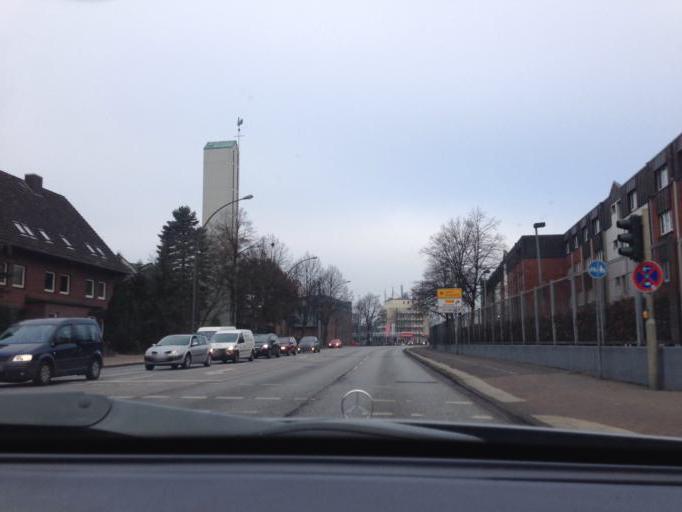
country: DE
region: Hamburg
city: Farmsen-Berne
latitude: 53.5843
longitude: 10.1256
